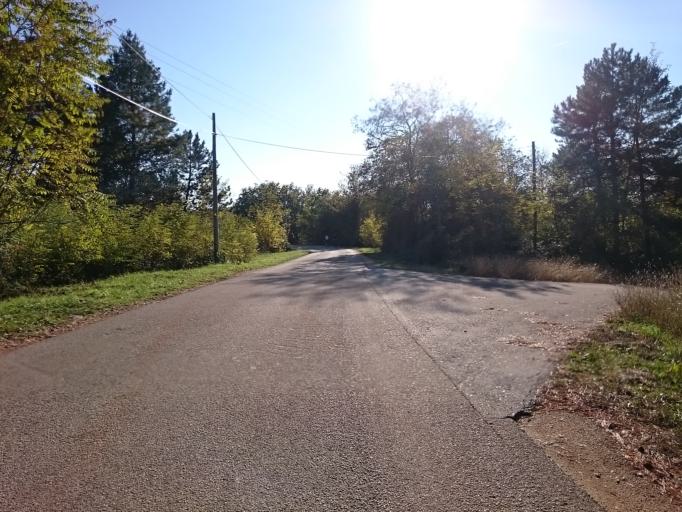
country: HR
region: Istarska
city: Buje
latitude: 45.4144
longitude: 13.7210
